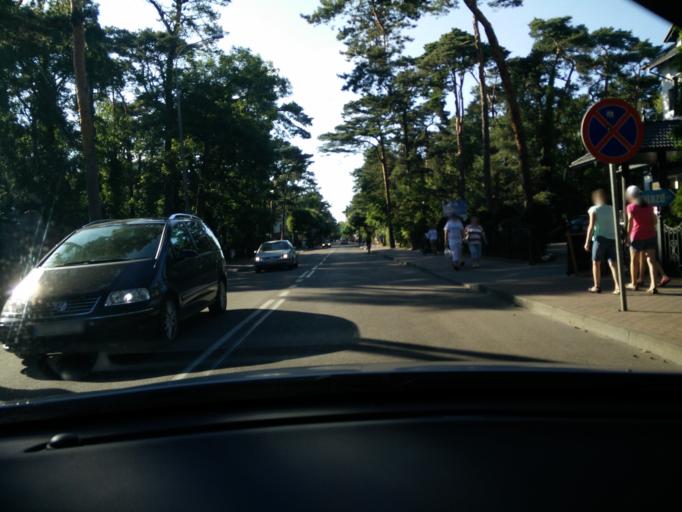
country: PL
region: Pomeranian Voivodeship
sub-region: Powiat pucki
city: Jastarnia
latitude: 54.6815
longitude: 18.7171
